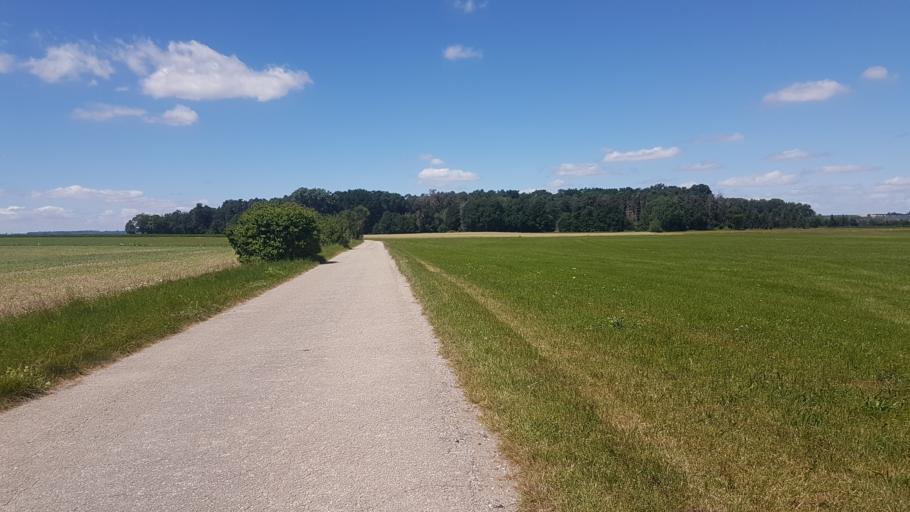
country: DE
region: Bavaria
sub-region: Regierungsbezirk Mittelfranken
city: Aurach
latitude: 49.2730
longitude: 10.4308
